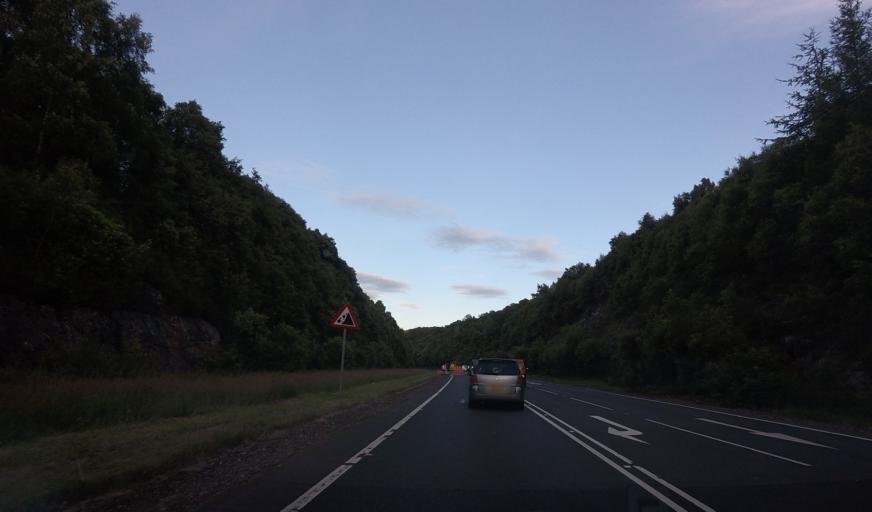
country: GB
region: Scotland
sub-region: Argyll and Bute
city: Helensburgh
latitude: 56.1694
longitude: -4.6773
